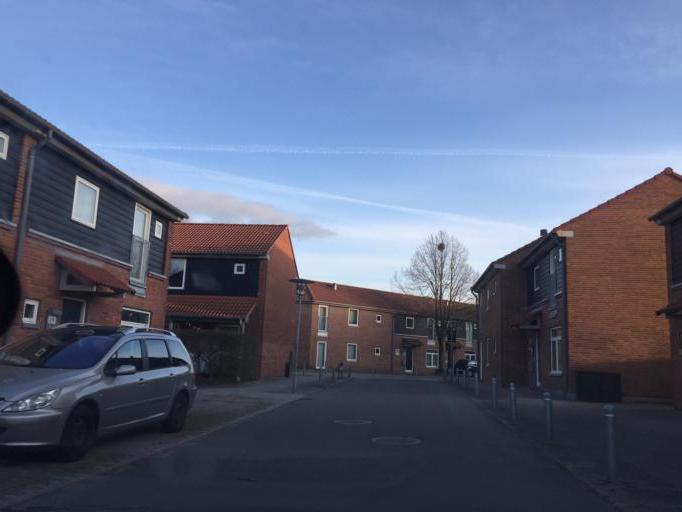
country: DK
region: South Denmark
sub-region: Odense Kommune
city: Neder Holluf
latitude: 55.3776
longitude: 10.4615
